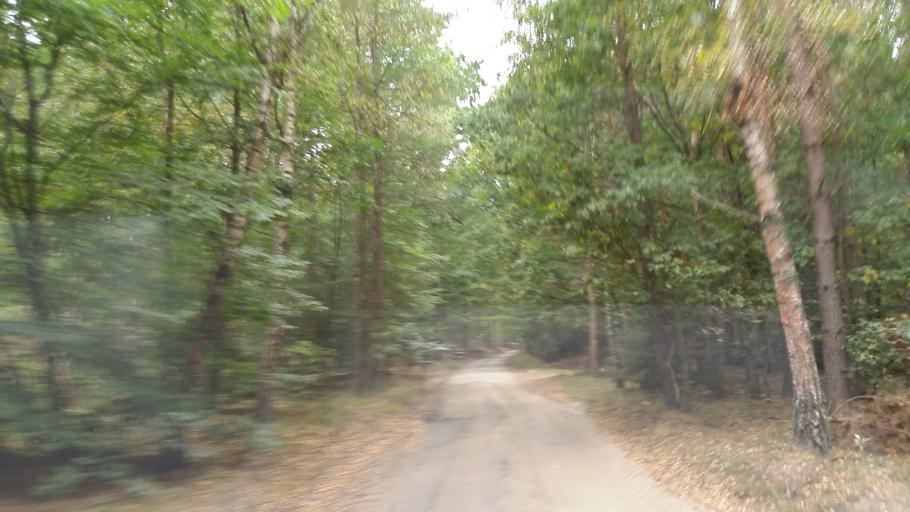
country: PL
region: West Pomeranian Voivodeship
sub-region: Powiat mysliborski
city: Barlinek
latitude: 52.9589
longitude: 15.2813
